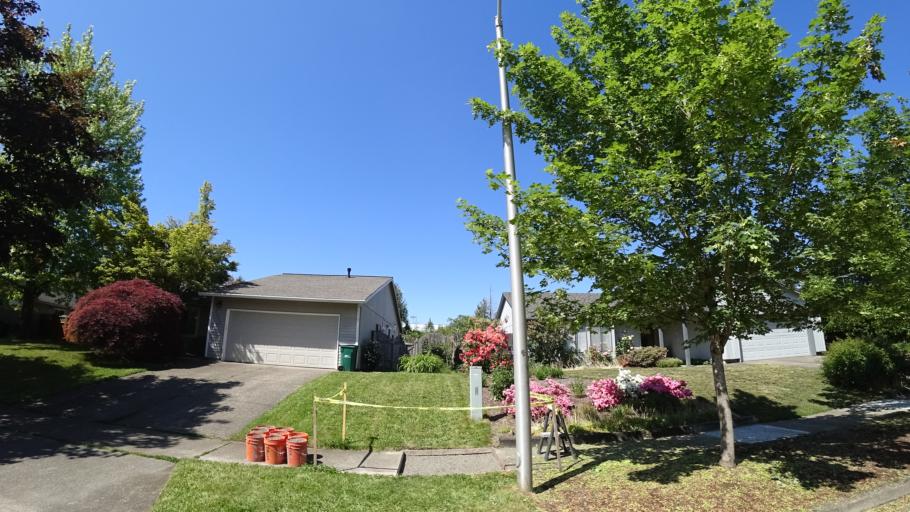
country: US
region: Oregon
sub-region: Washington County
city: Beaverton
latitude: 45.4473
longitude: -122.8096
